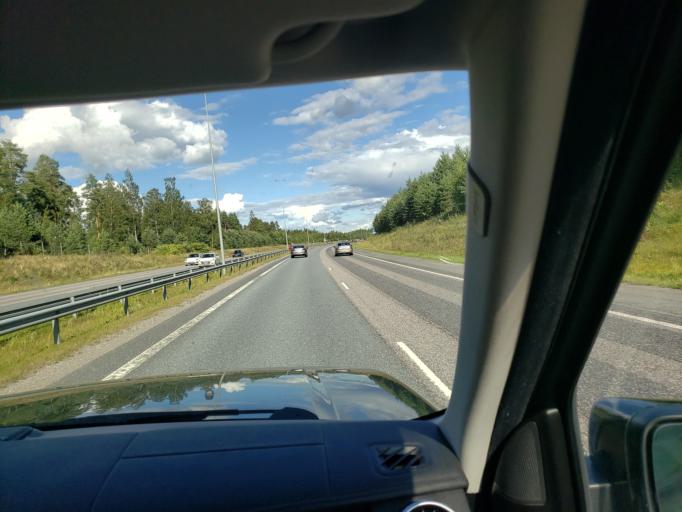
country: FI
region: Uusimaa
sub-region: Helsinki
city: Lohja
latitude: 60.3019
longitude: 24.1976
